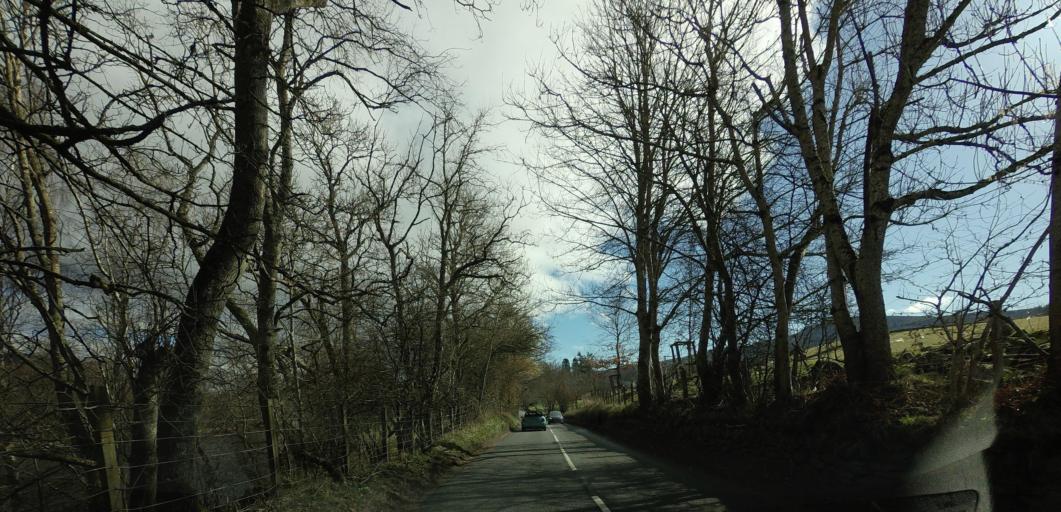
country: GB
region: Scotland
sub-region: Perth and Kinross
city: Aberfeldy
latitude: 56.6170
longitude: -3.8837
